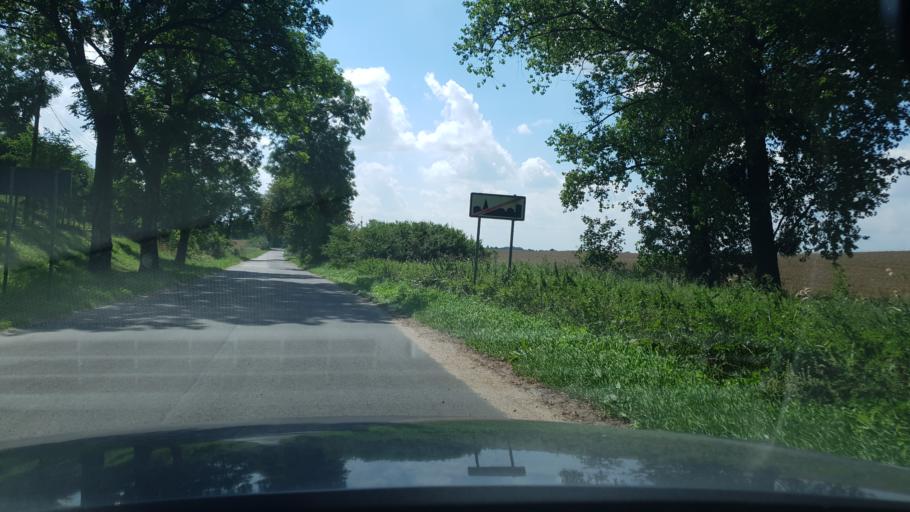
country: PL
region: Kujawsko-Pomorskie
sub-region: Powiat wabrzeski
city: Pluznica
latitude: 53.3441
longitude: 18.8274
